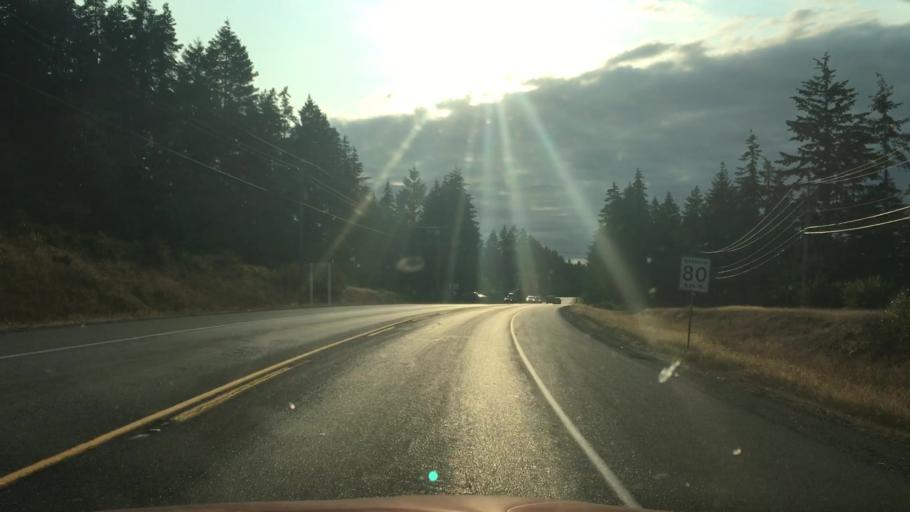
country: CA
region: British Columbia
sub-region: Regional District of Nanaimo
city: Parksville
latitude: 49.3033
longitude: -124.4578
